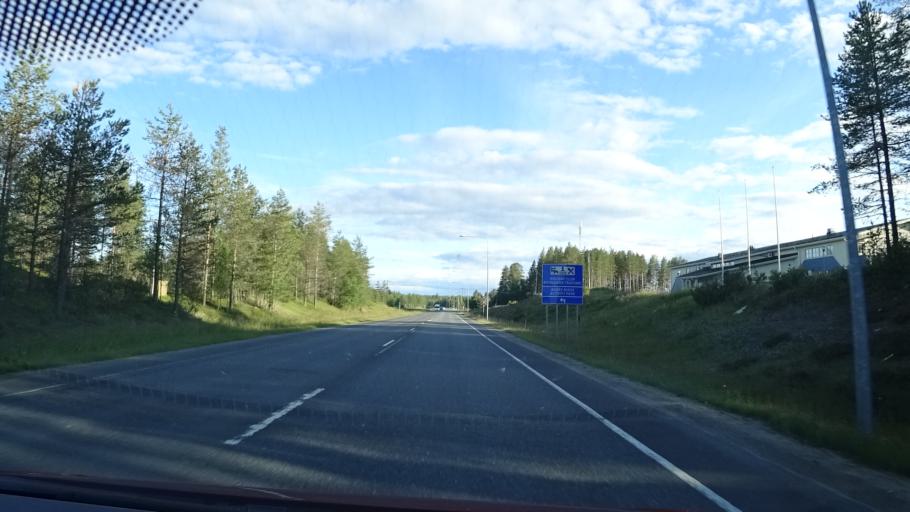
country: FI
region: Northern Ostrobothnia
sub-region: Koillismaa
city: Kuusamo
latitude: 66.0025
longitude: 29.1521
